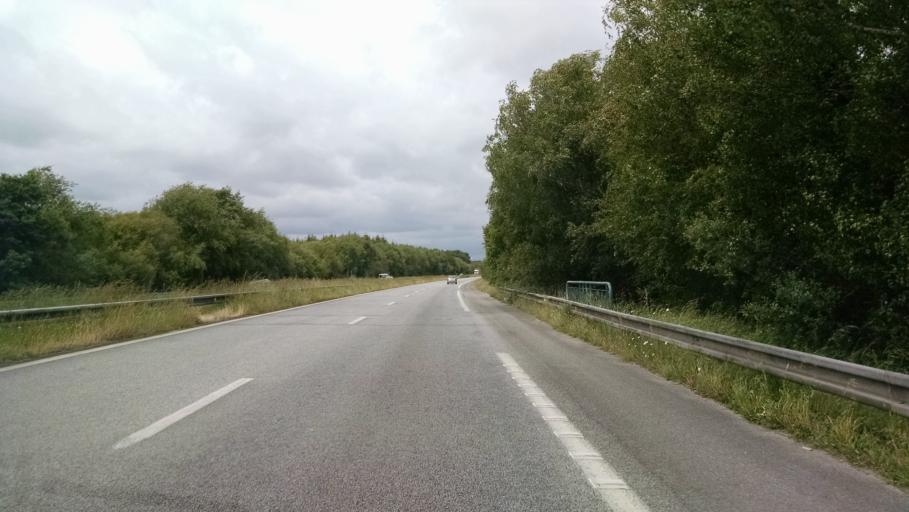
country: FR
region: Brittany
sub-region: Departement du Morbihan
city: Gestel
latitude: 47.7972
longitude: -3.4539
